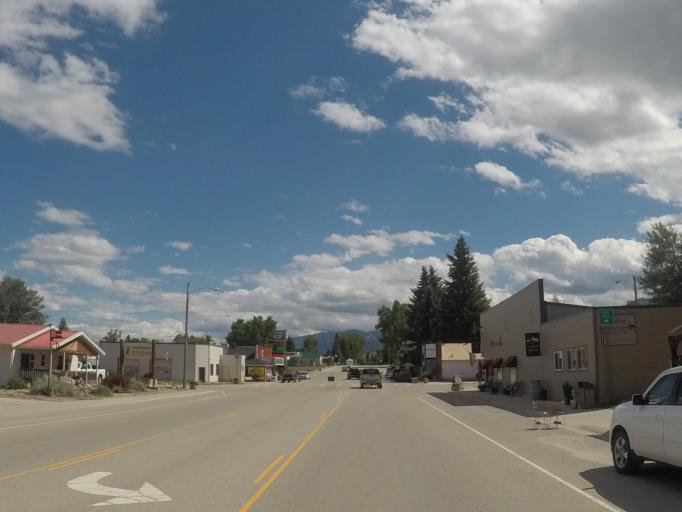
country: US
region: Wyoming
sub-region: Sheridan County
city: Sheridan
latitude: 44.8768
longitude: -107.2628
